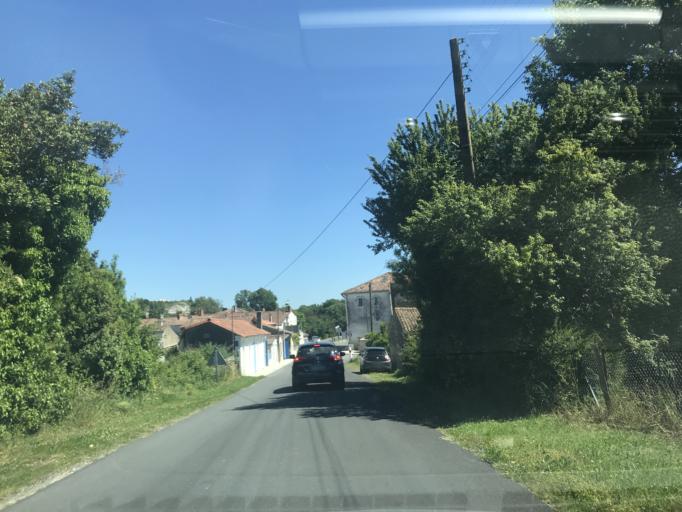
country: FR
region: Poitou-Charentes
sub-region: Departement de la Charente-Maritime
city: Mortagne-sur-Gironde
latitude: 45.4784
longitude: -0.7936
